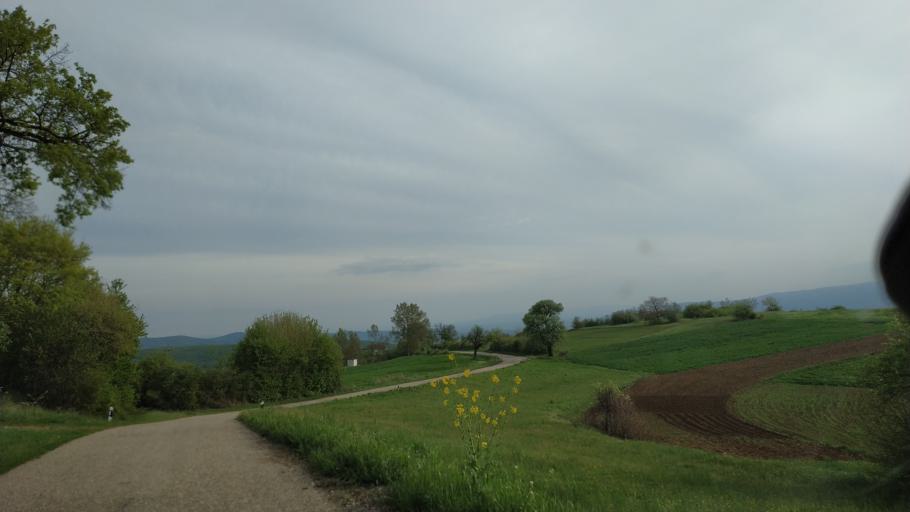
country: RS
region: Central Serbia
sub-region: Zajecarski Okrug
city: Soko Banja
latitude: 43.5383
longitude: 21.8795
